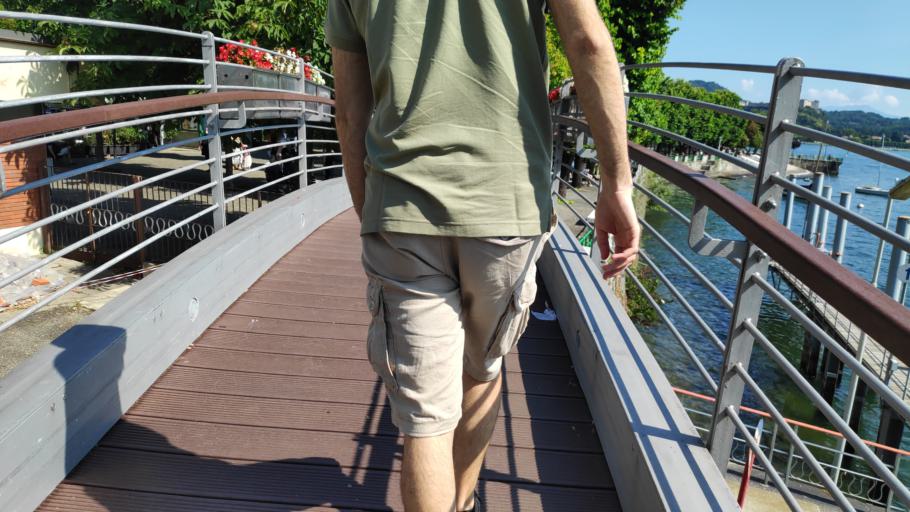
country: IT
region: Piedmont
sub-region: Provincia di Novara
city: Arona
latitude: 45.7587
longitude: 8.5615
